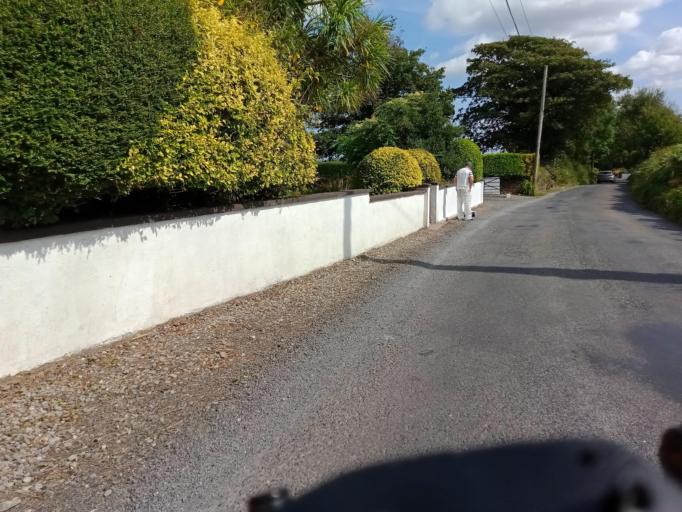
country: IE
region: Munster
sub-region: Waterford
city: Dungarvan
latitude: 52.1200
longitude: -7.4871
